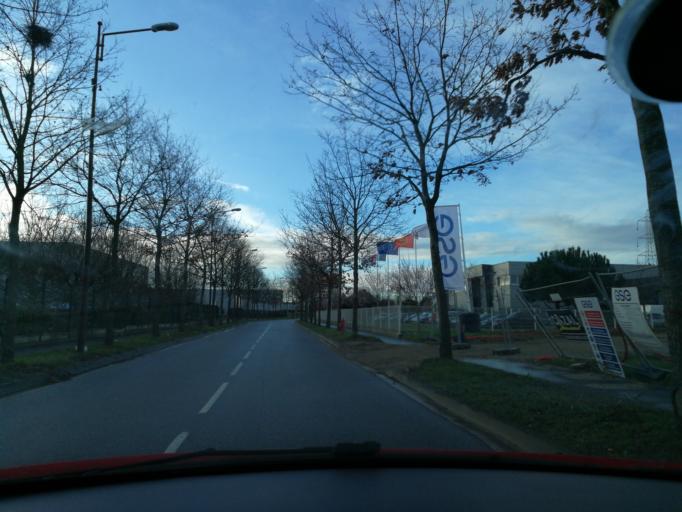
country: FR
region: Midi-Pyrenees
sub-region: Departement de la Haute-Garonne
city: Blagnac
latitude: 43.6389
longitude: 1.4165
